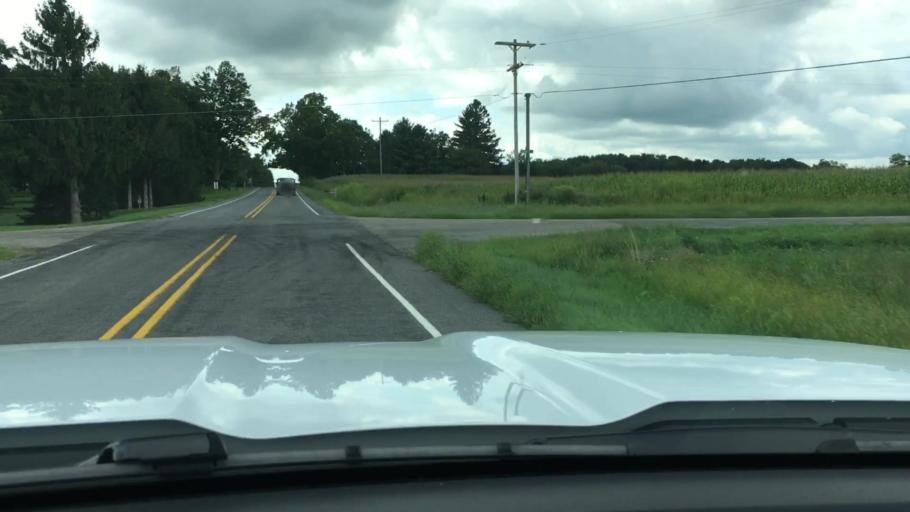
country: US
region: Michigan
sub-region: Ingham County
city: Holt
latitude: 42.5533
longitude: -84.5622
